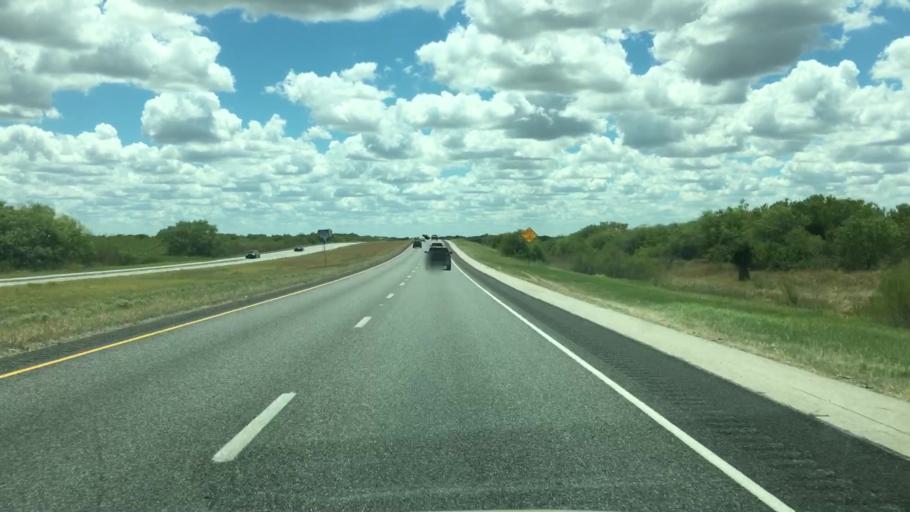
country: US
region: Texas
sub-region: Atascosa County
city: Pleasanton
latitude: 29.0907
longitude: -98.4331
